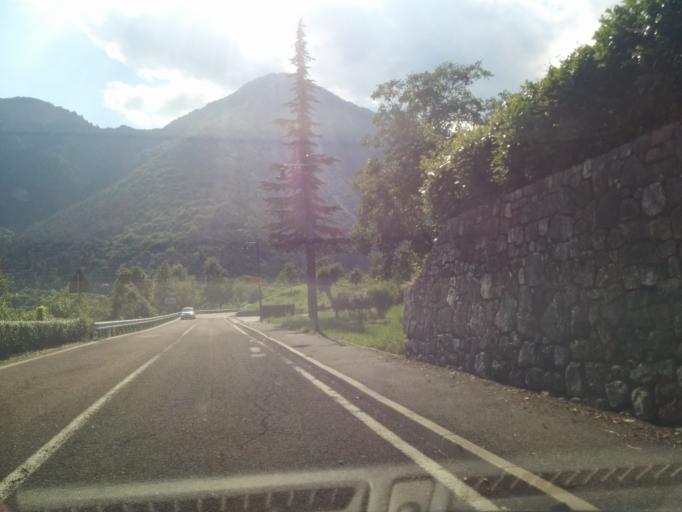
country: IT
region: Trentino-Alto Adige
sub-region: Provincia di Trento
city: Tenno
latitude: 45.9297
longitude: 10.8200
